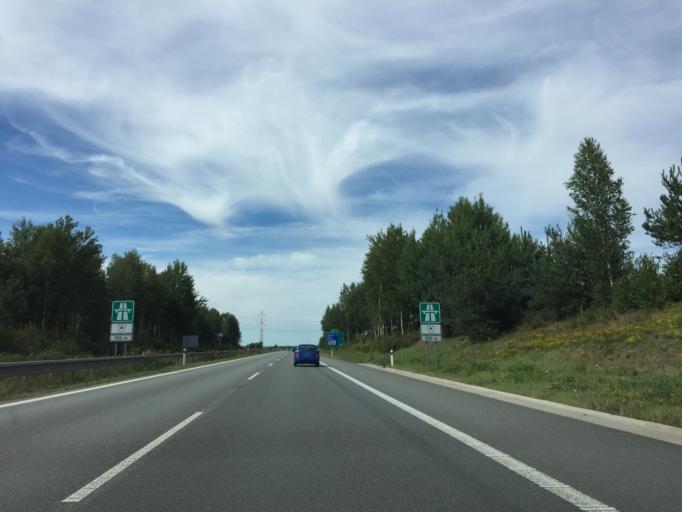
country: CZ
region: Jihocesky
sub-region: Okres Tabor
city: Sezimovo Usti
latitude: 49.4229
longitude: 14.7029
